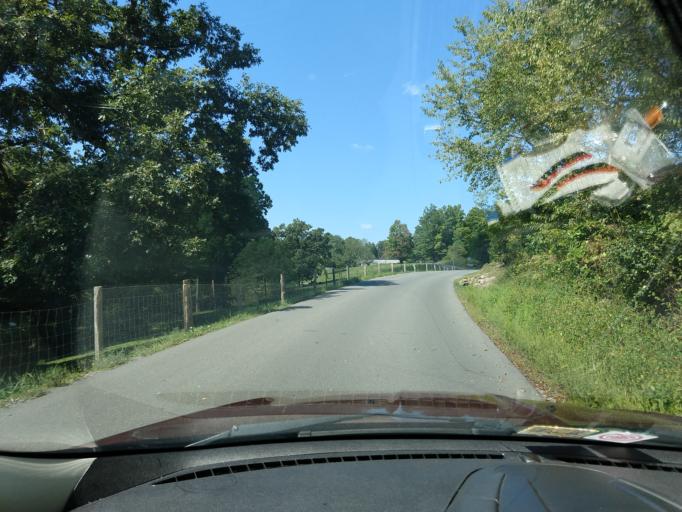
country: US
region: West Virginia
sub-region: Nicholas County
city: Craigsville
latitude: 38.2817
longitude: -80.7435
